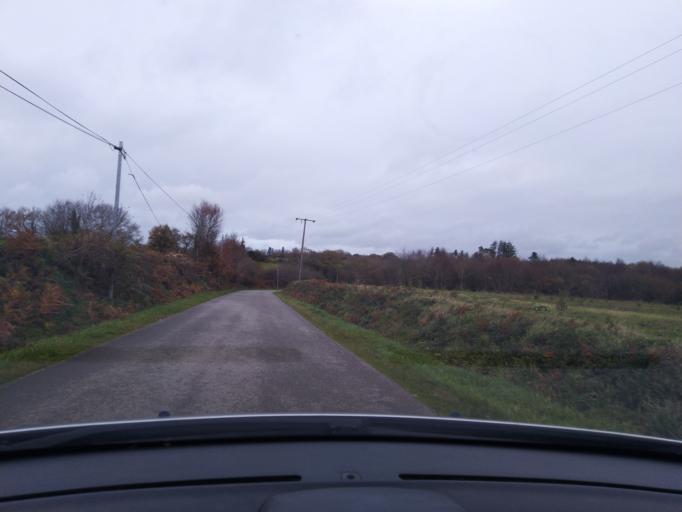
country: FR
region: Brittany
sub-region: Departement du Finistere
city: Guerlesquin
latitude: 48.5322
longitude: -3.5655
